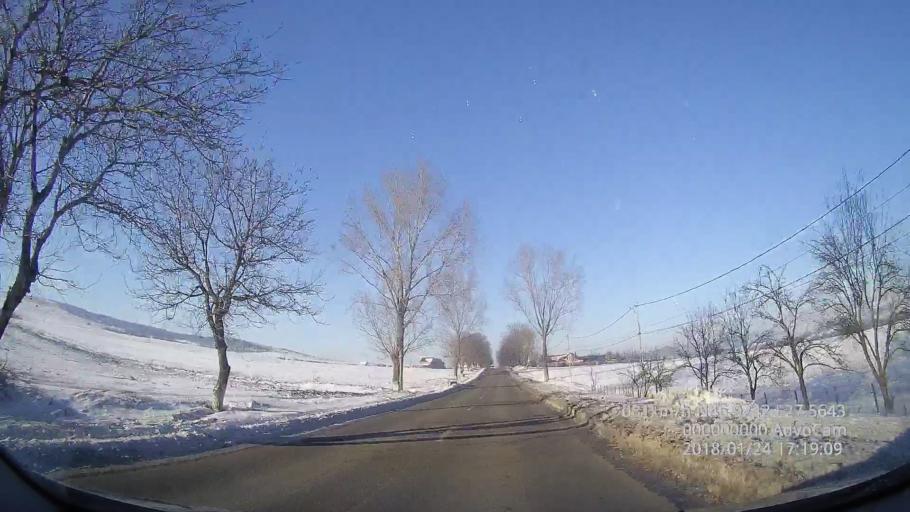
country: RO
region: Iasi
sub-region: Comuna Scanteia
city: Scanteia
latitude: 46.9248
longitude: 27.5642
